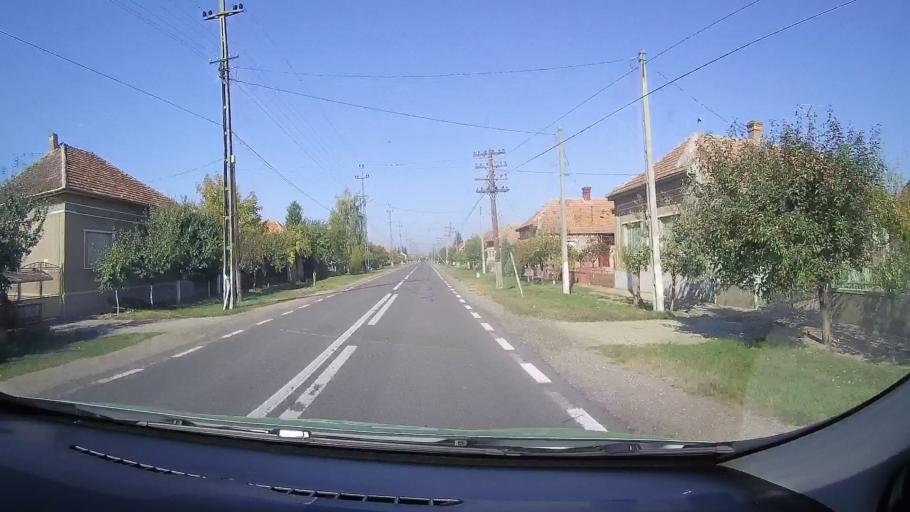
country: RO
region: Satu Mare
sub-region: Comuna Urziceni
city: Urziceni
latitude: 47.7272
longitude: 22.4089
